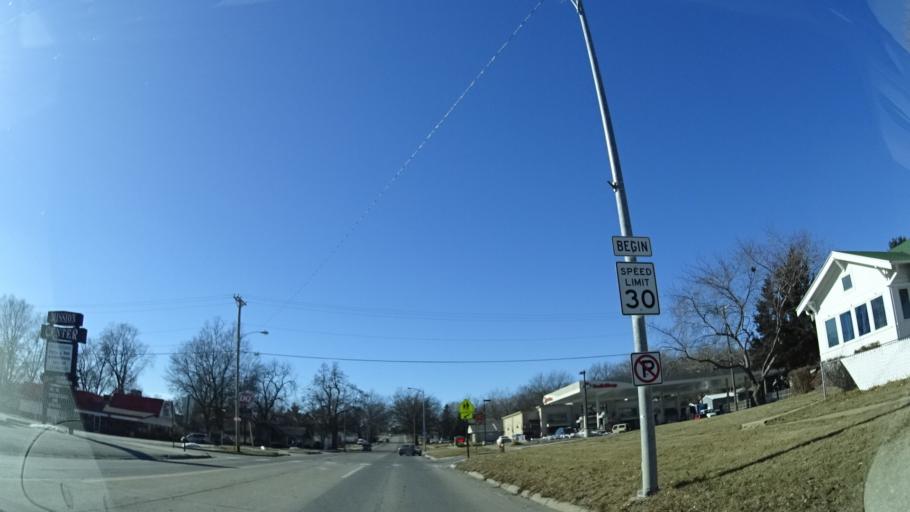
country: US
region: Nebraska
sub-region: Sarpy County
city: Bellevue
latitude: 41.1365
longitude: -95.8985
